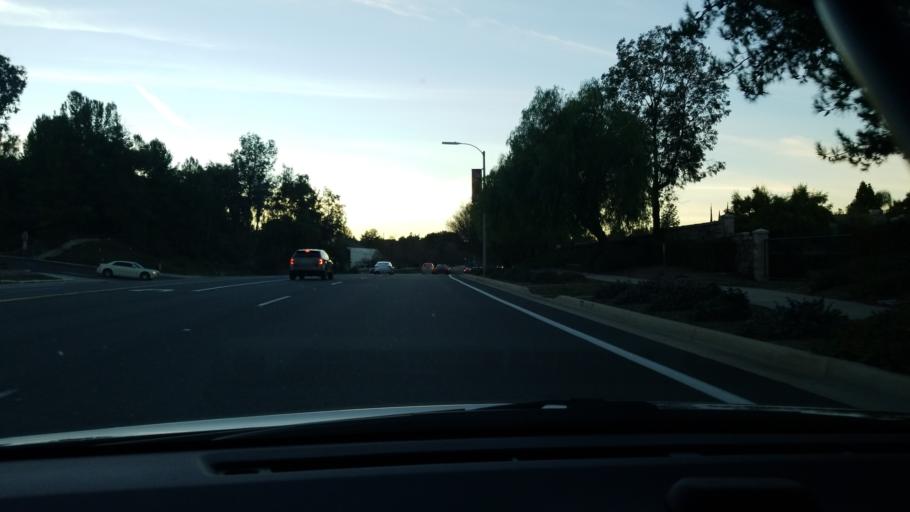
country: US
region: California
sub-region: Riverside County
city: Temecula
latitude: 33.5076
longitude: -117.1204
